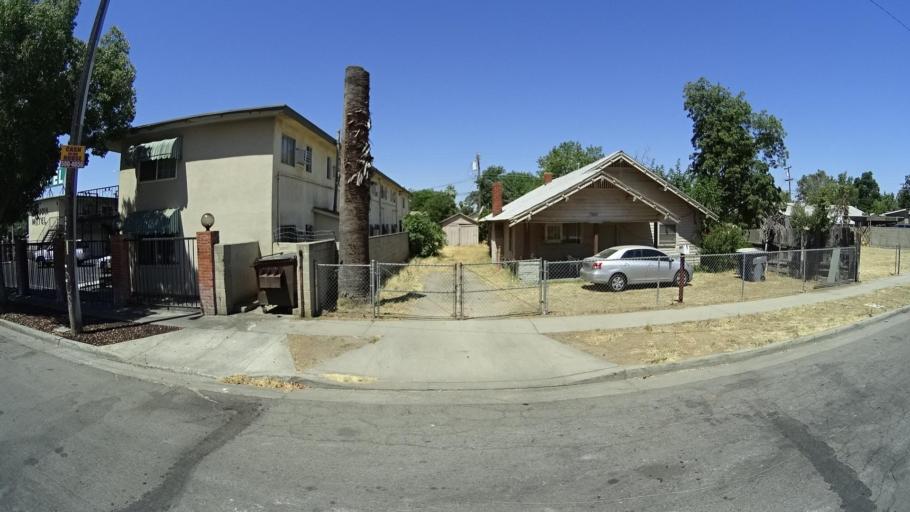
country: US
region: California
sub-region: Fresno County
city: Fresno
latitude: 36.7363
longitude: -119.7404
